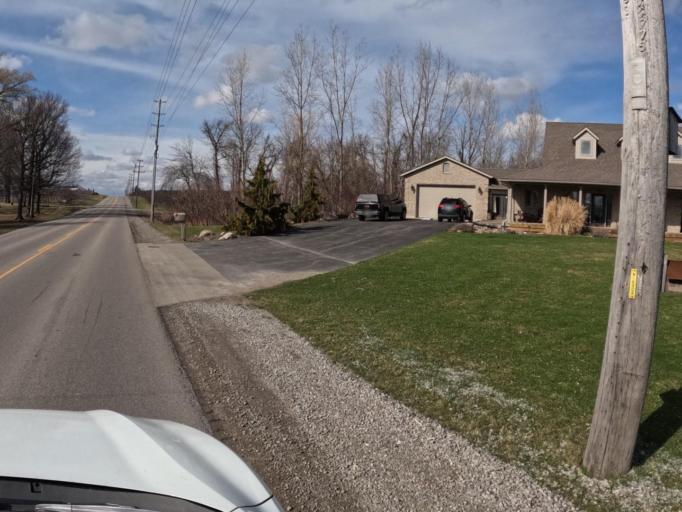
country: CA
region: Ontario
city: Norfolk County
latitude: 42.8574
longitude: -80.2651
